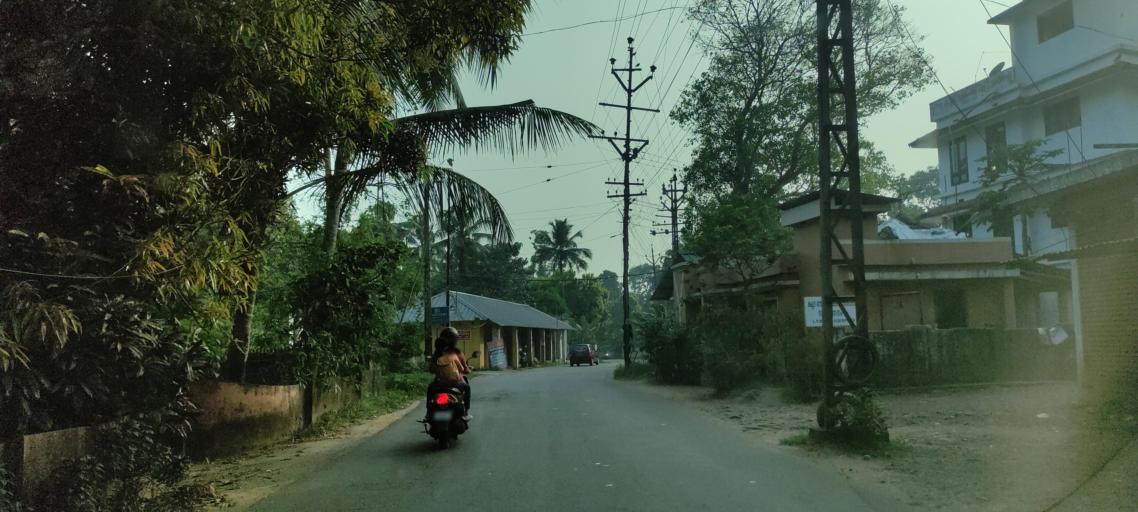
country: IN
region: Kerala
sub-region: Kottayam
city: Vaikam
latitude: 9.7180
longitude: 76.4762
